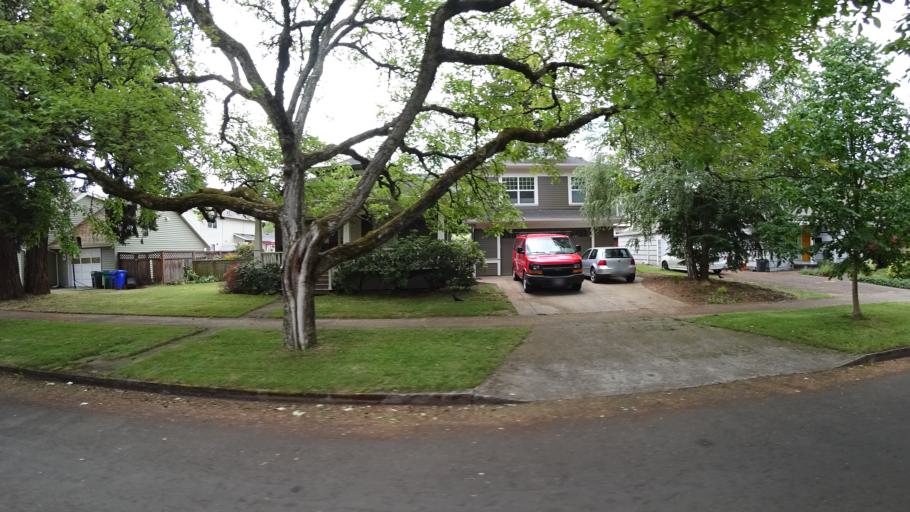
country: US
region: Oregon
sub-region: Washington County
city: West Haven
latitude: 45.5818
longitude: -122.7272
